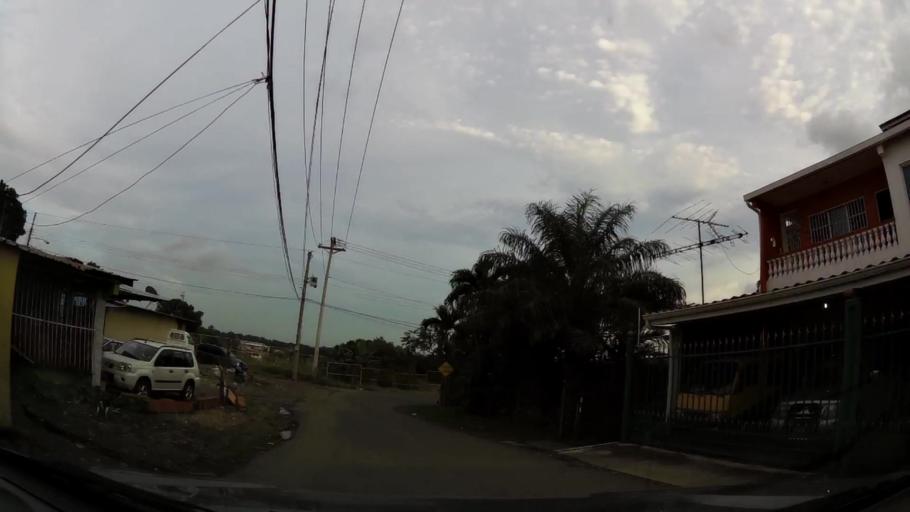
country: PA
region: Panama
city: Tocumen
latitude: 9.0920
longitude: -79.3945
